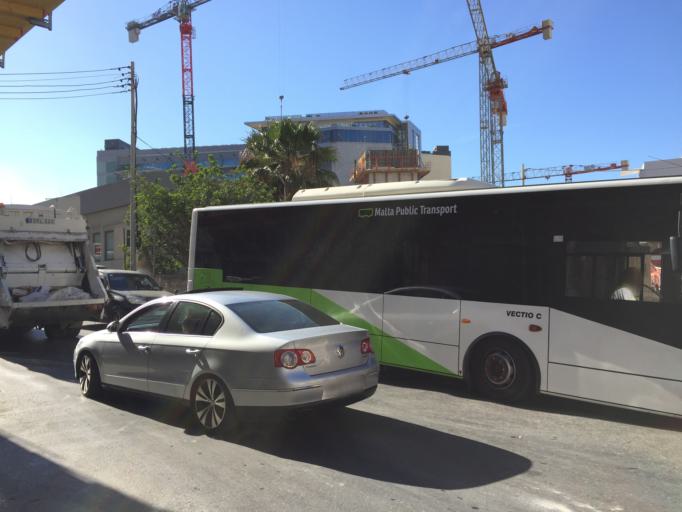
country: MT
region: Saint Julian
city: San Giljan
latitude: 35.9221
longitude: 14.4901
